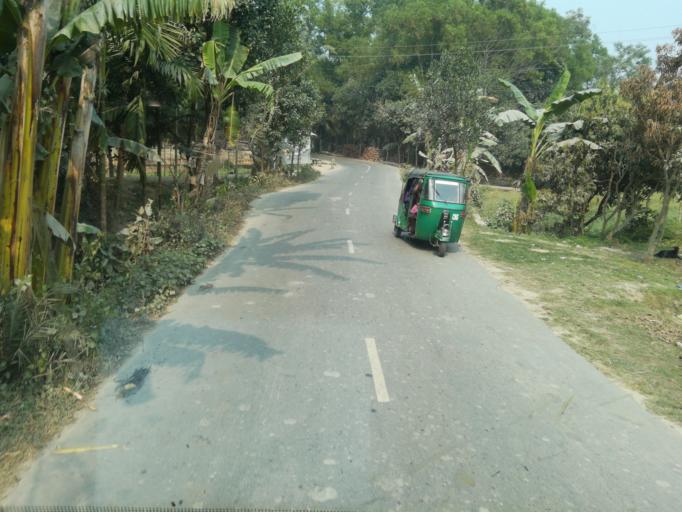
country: BD
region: Dhaka
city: Nagarpur
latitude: 23.9900
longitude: 89.8468
